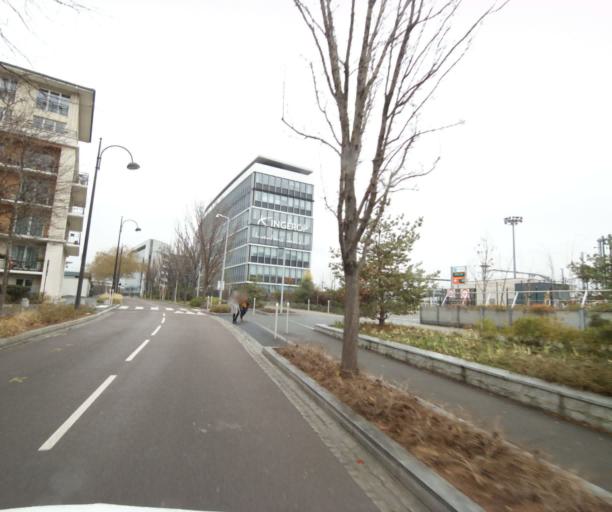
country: FR
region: Ile-de-France
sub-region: Departement des Yvelines
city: Chatou
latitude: 48.8891
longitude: 2.1748
